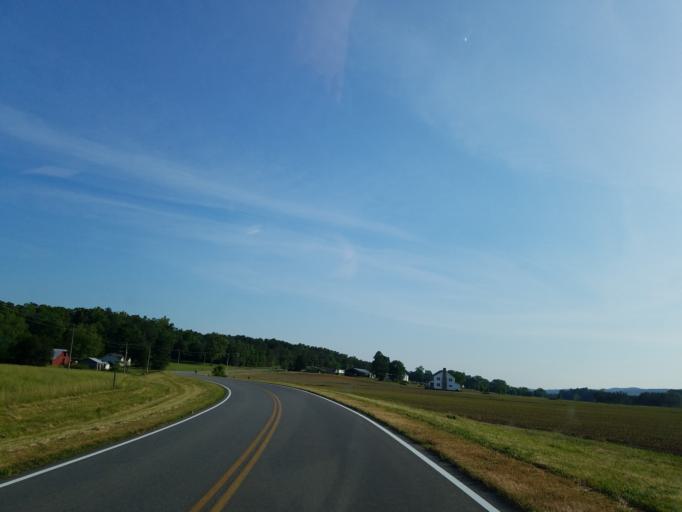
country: US
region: Georgia
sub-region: Chattooga County
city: Trion
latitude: 34.5160
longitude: -85.2308
